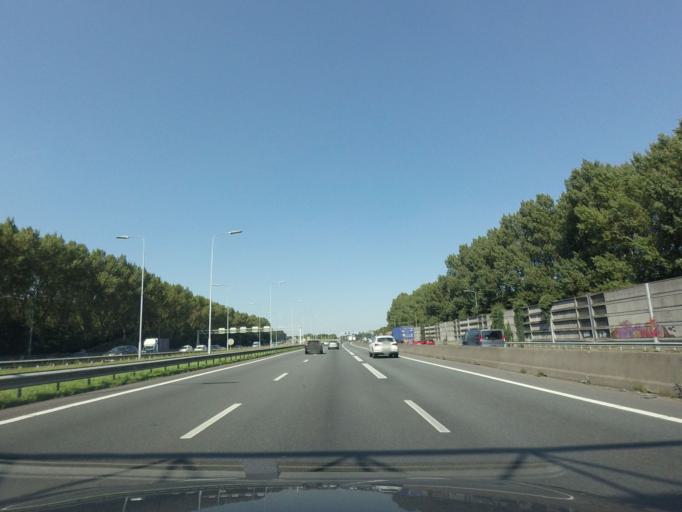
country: NL
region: South Holland
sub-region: Gemeente Rotterdam
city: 's-Gravenland
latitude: 51.9428
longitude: 4.5333
